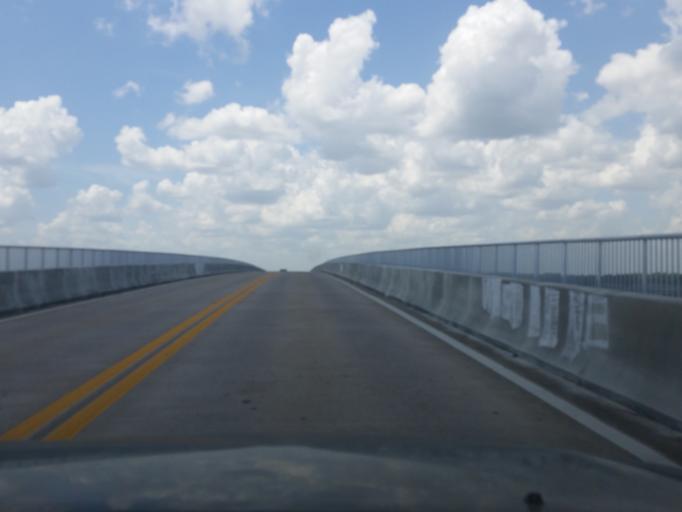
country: US
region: Florida
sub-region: Santa Rosa County
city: Navarre
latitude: 30.3961
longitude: -86.8632
